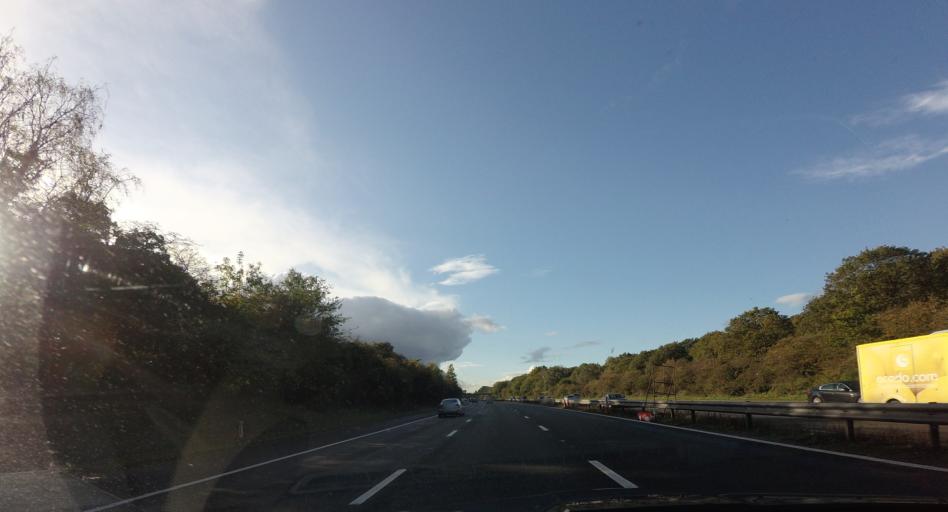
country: GB
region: England
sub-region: Kent
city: Dartford
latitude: 51.4322
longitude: 0.1961
